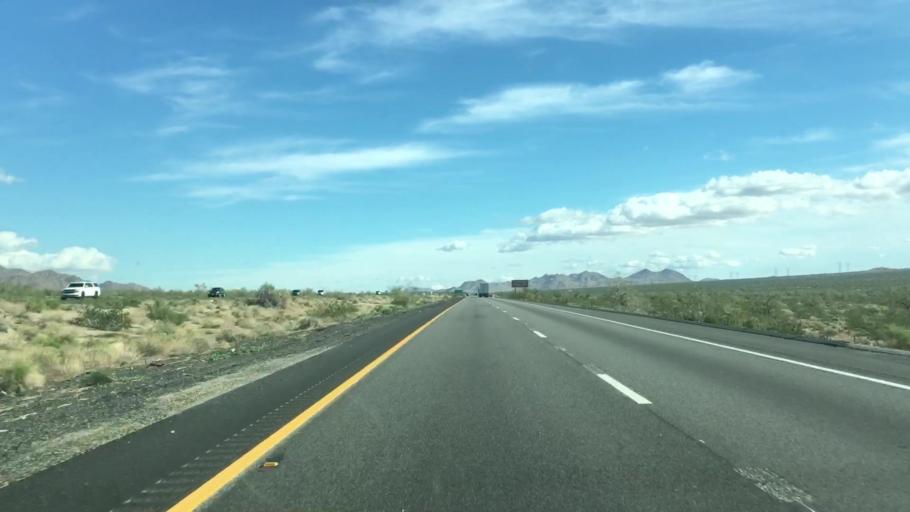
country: US
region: California
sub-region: Riverside County
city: Mecca
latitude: 33.6609
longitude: -115.8224
